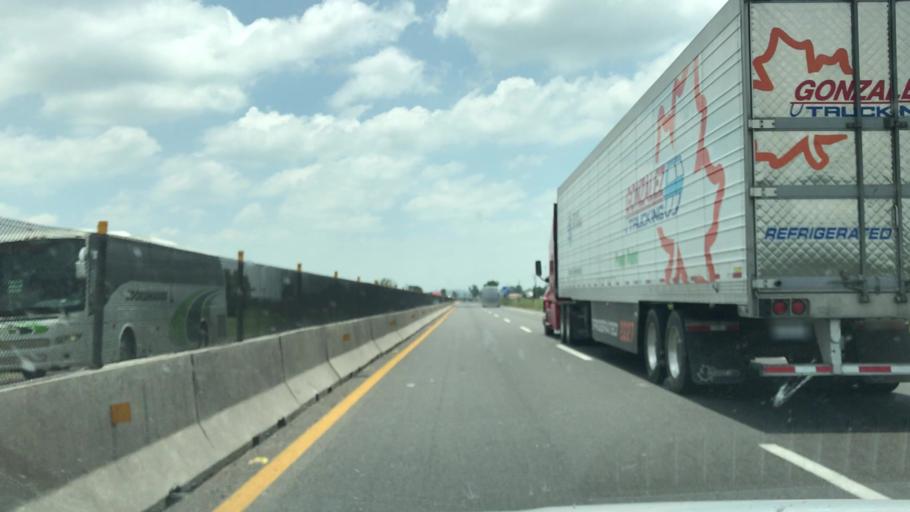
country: MX
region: Guanajuato
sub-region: Abasolo
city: San Bernardo Pena Blanca
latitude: 20.4835
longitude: -101.4939
